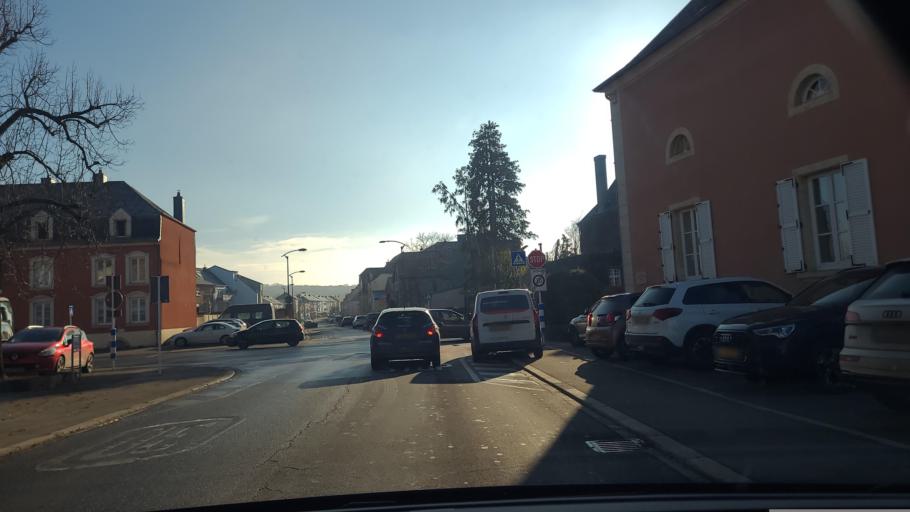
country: LU
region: Luxembourg
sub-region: Canton de Capellen
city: Bascharage
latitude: 49.5654
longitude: 5.9069
